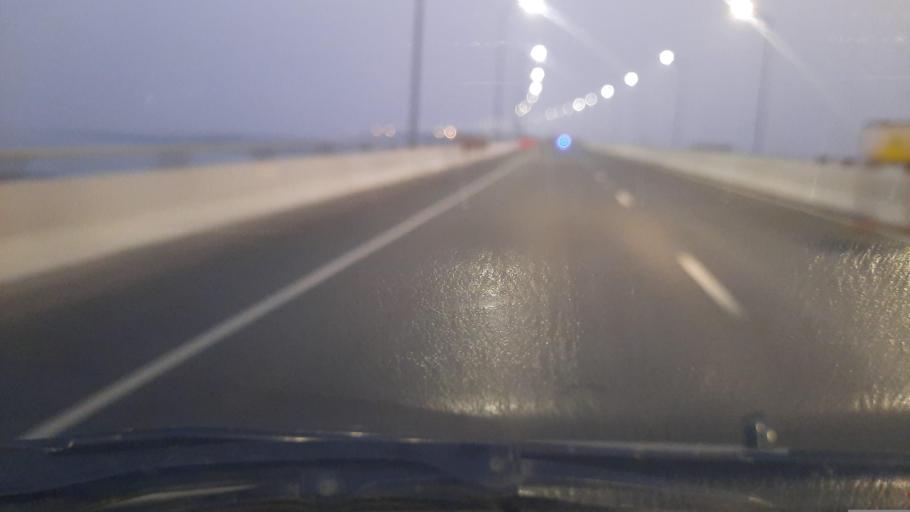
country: BD
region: Dhaka
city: Char Bhadrasan
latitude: 23.4146
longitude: 90.2586
